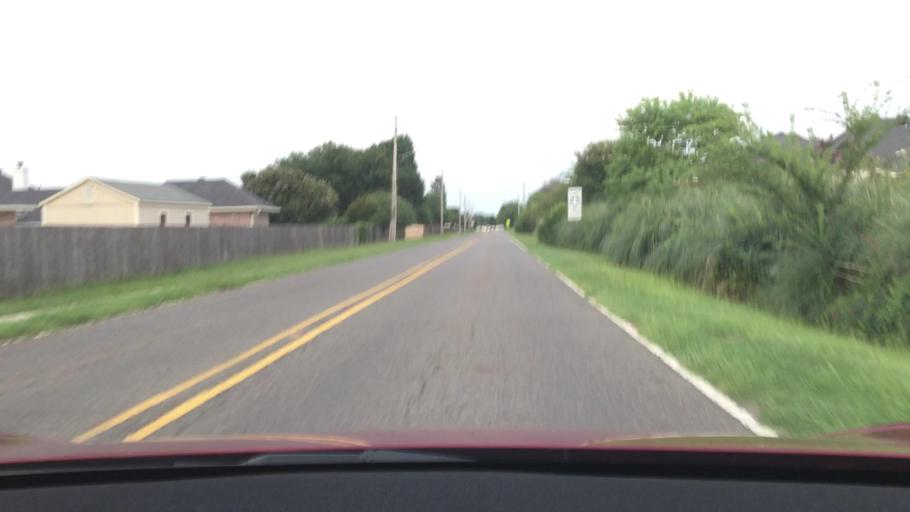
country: US
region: Louisiana
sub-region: Bossier Parish
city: Bossier City
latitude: 32.4533
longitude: -93.6696
